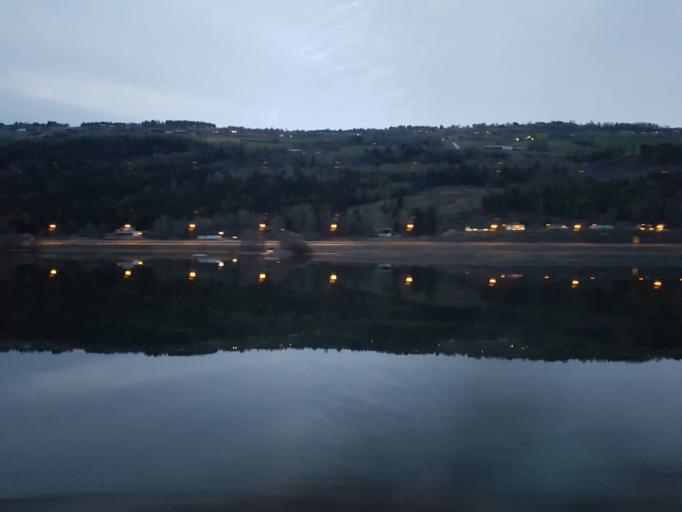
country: NO
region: Oppland
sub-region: Oyer
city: Tretten
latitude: 61.2680
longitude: 10.3986
